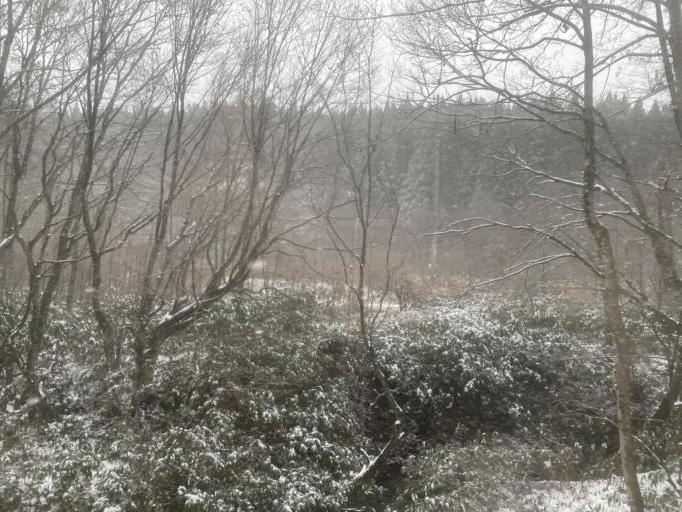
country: JP
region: Aomori
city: Goshogawara
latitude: 41.1141
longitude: 140.5286
